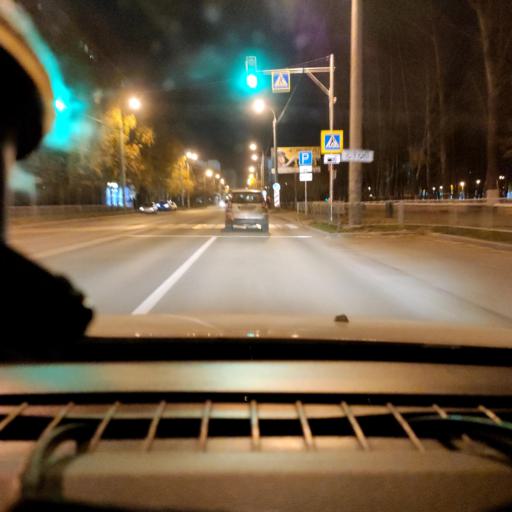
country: RU
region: Samara
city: Samara
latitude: 53.2271
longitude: 50.2032
